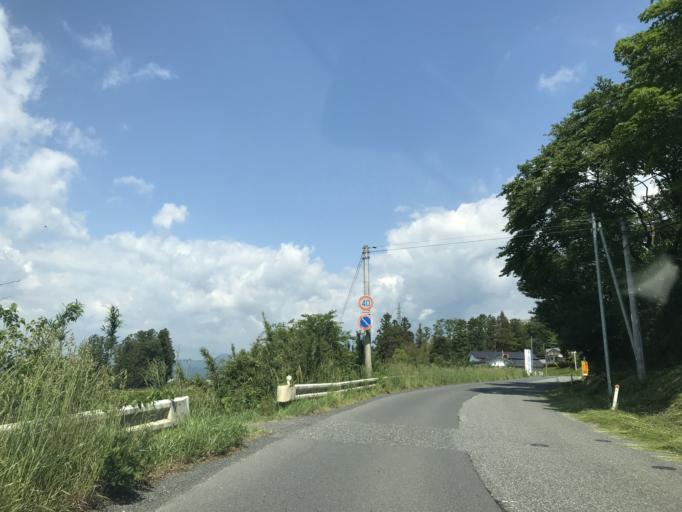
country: JP
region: Iwate
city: Ichinoseki
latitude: 38.8036
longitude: 141.0064
